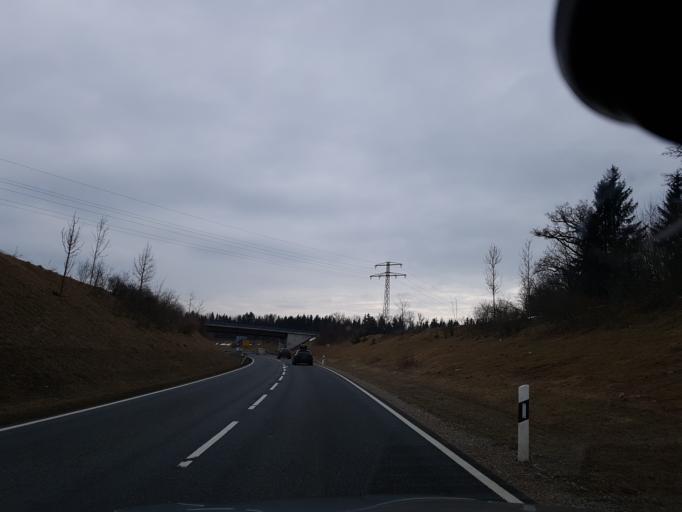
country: DE
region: Bavaria
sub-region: Upper Bavaria
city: Brunnthal
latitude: 48.0141
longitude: 11.6980
